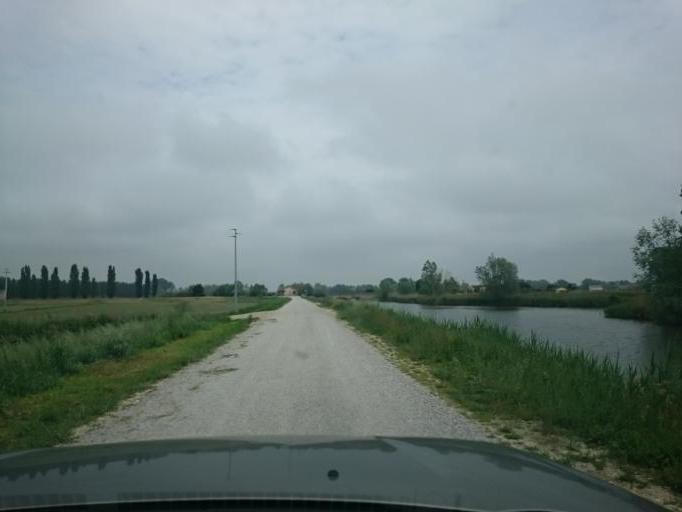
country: IT
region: Veneto
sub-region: Provincia di Venezia
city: Valli
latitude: 45.2183
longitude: 12.1530
